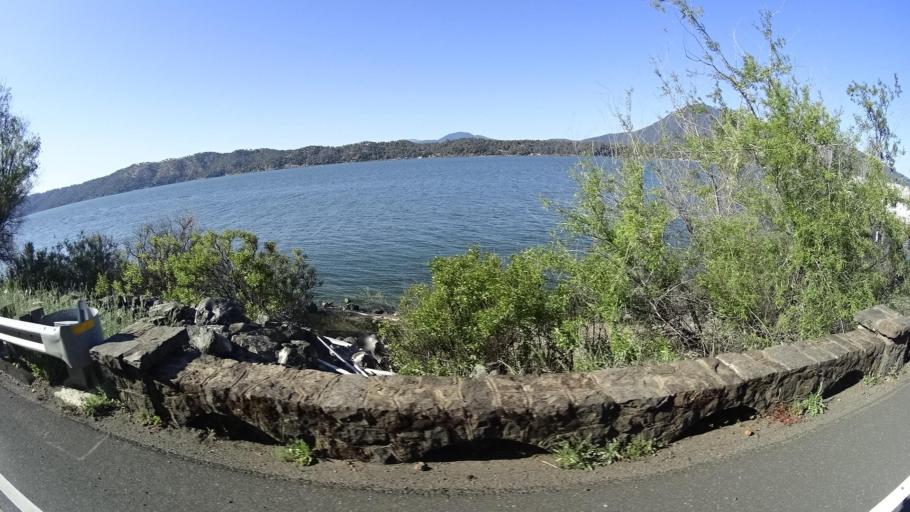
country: US
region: California
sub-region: Lake County
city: Clearlake Oaks
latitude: 39.0205
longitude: -122.7062
